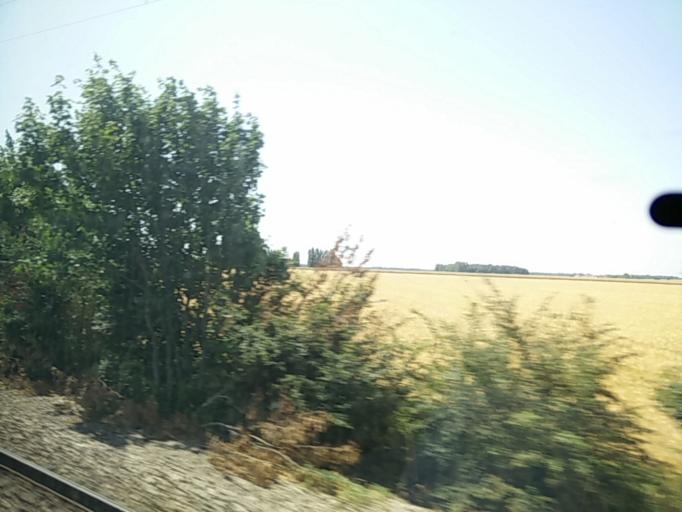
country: FR
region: Ile-de-France
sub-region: Departement de Seine-et-Marne
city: Bailly-Carrois
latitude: 48.5756
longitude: 2.9932
